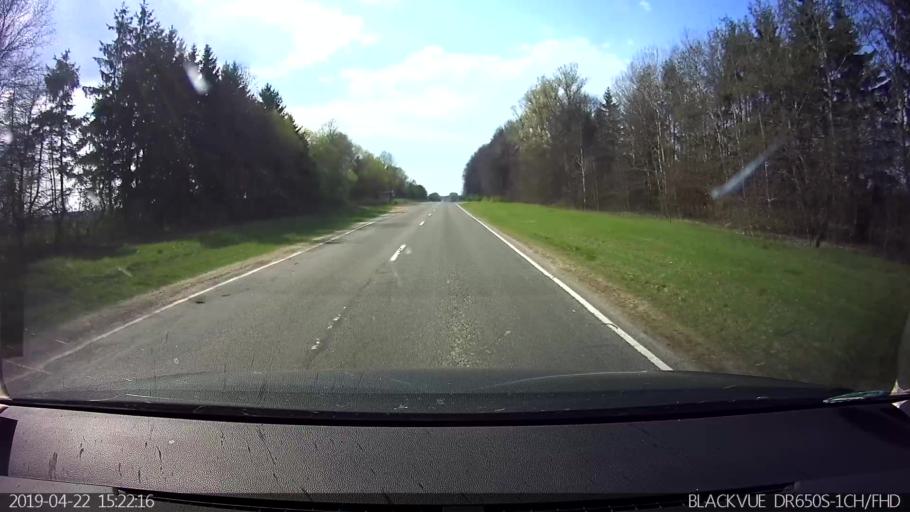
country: BY
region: Brest
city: Vysokaye
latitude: 52.3489
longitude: 23.4501
